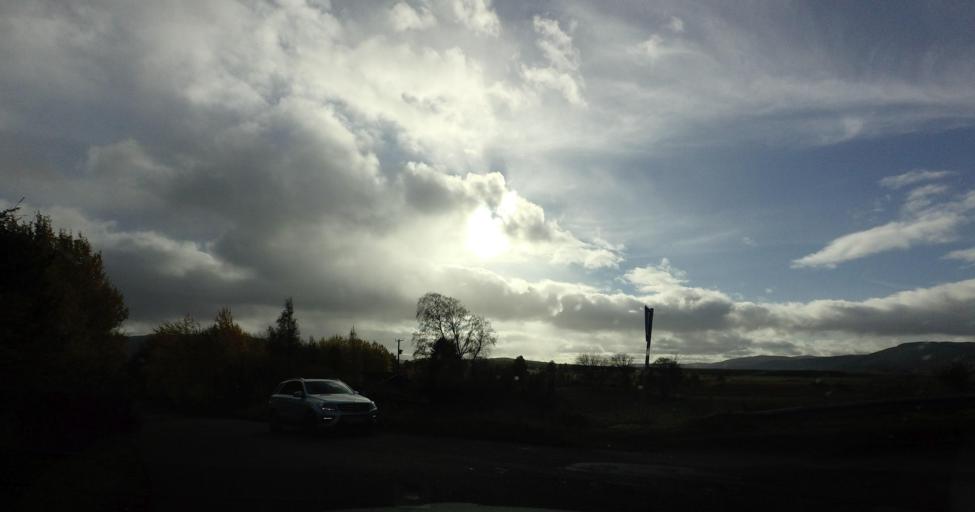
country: GB
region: Scotland
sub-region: Highland
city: Aviemore
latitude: 57.2581
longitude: -3.7536
